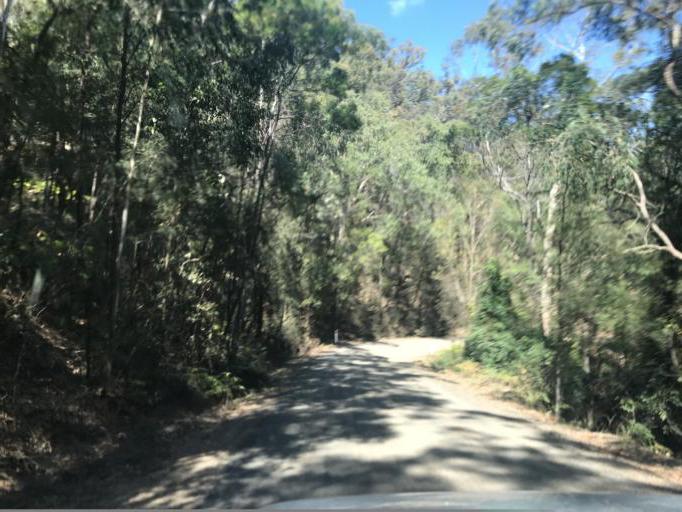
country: AU
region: New South Wales
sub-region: Wyong Shire
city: Little Jilliby
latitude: -33.1536
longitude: 151.0802
